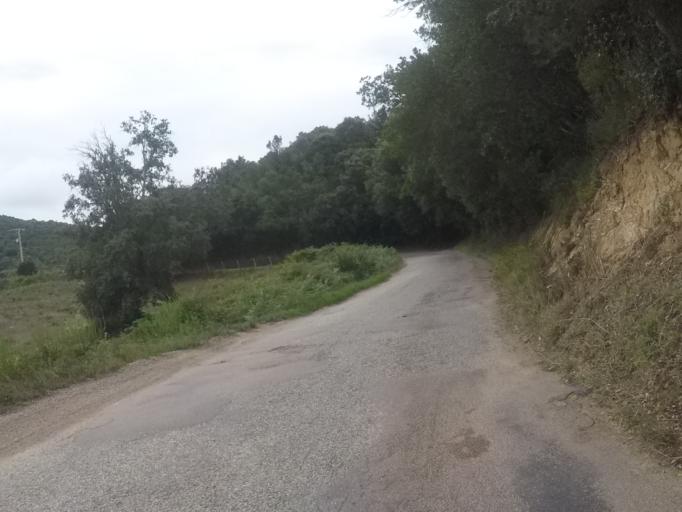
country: FR
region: Corsica
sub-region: Departement de la Corse-du-Sud
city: Pietrosella
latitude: 41.8130
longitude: 8.8504
